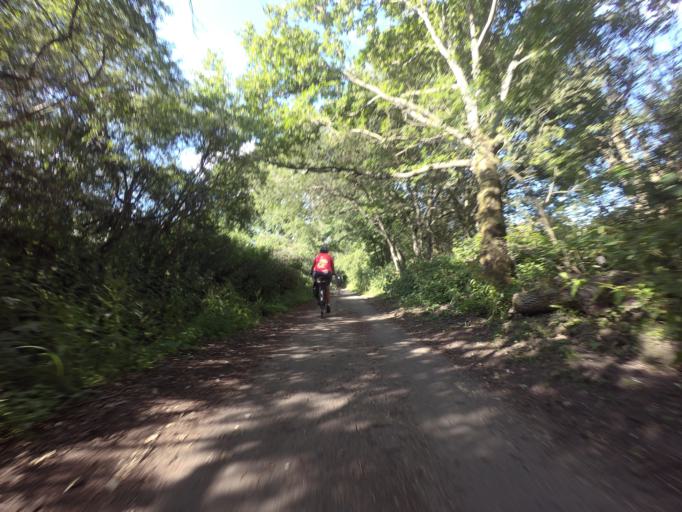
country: GB
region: England
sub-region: East Sussex
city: Hailsham
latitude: 50.8970
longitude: 0.2573
